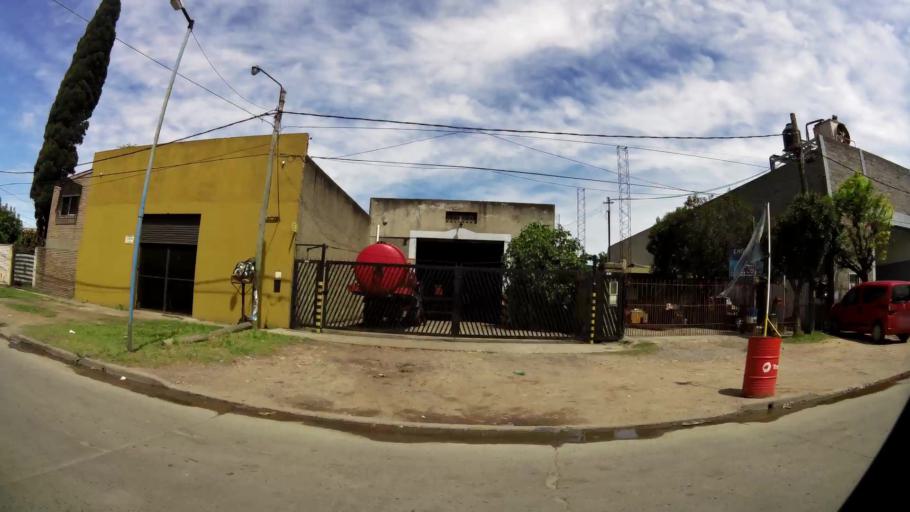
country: AR
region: Buenos Aires
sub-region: Partido de Quilmes
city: Quilmes
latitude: -34.7576
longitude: -58.2988
